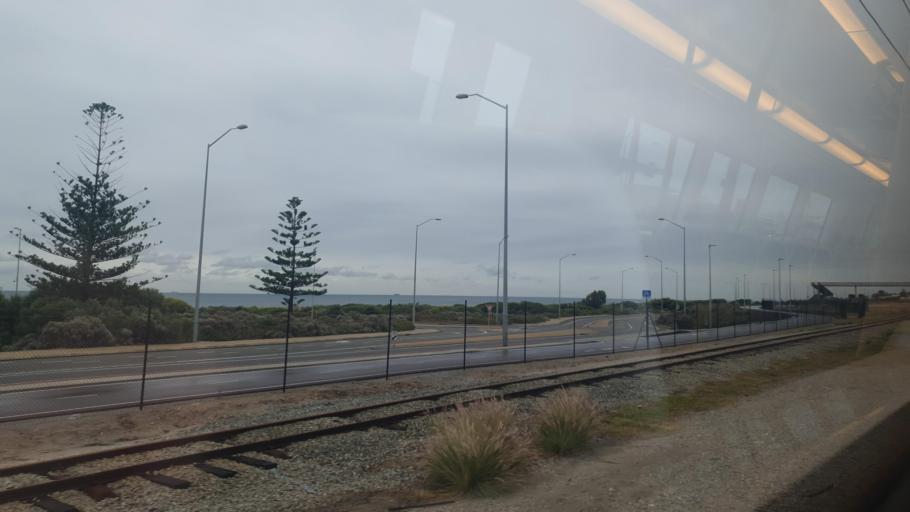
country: AU
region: Western Australia
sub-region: Fremantle
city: North Fremantle
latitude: -32.0271
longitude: 115.7520
